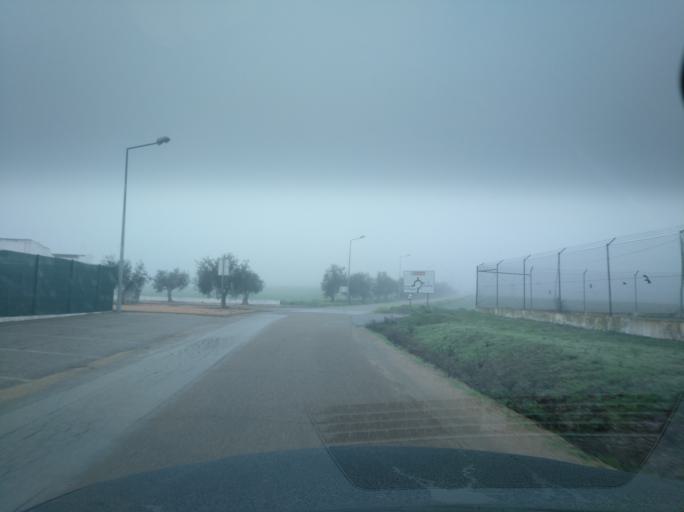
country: PT
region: Portalegre
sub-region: Campo Maior
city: Campo Maior
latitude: 39.0228
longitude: -7.0679
